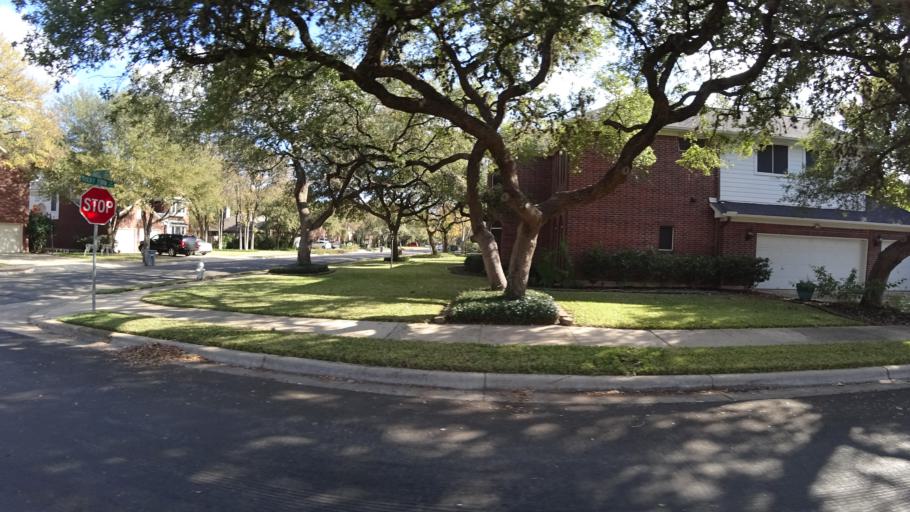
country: US
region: Texas
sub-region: Travis County
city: Shady Hollow
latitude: 30.1805
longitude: -97.8575
